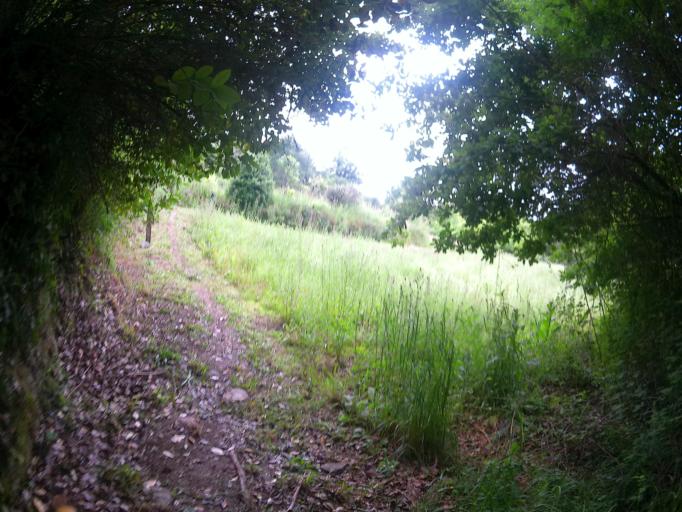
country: PT
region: Aveiro
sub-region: Albergaria-A-Velha
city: Branca
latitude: 40.7655
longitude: -8.4445
